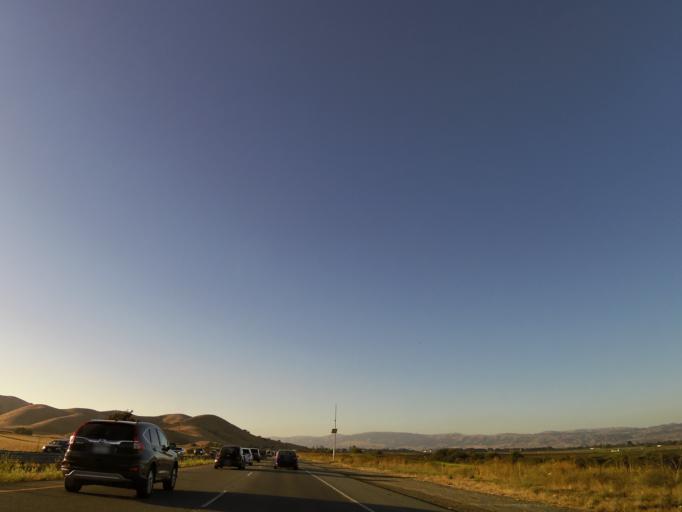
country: US
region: California
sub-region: Santa Clara County
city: Gilroy
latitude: 36.9378
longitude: -121.5525
